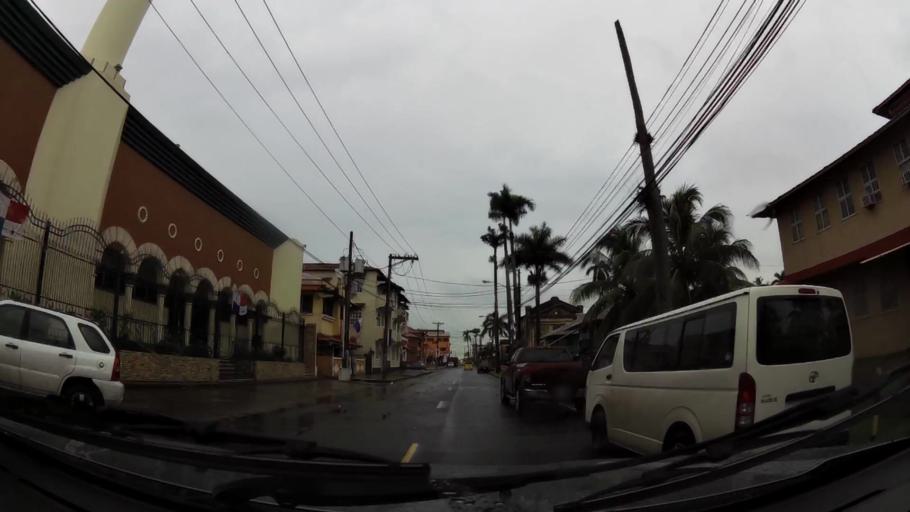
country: PA
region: Colon
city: Colon
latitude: 9.3634
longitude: -79.9011
